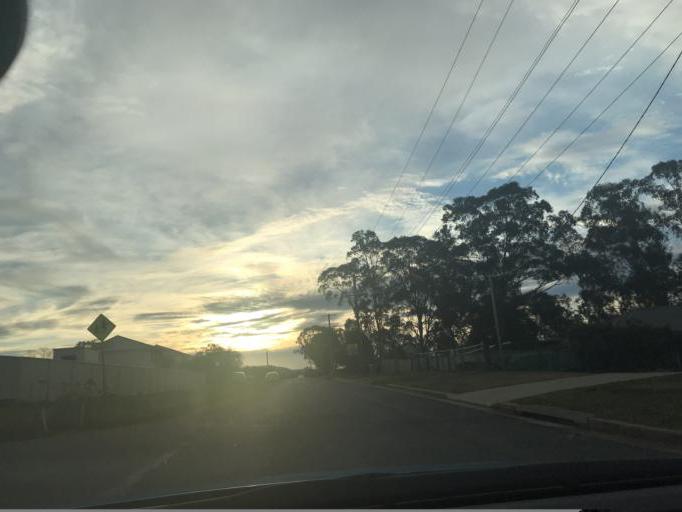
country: AU
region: New South Wales
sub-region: Cessnock
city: Cessnock
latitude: -32.9018
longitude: 151.2864
